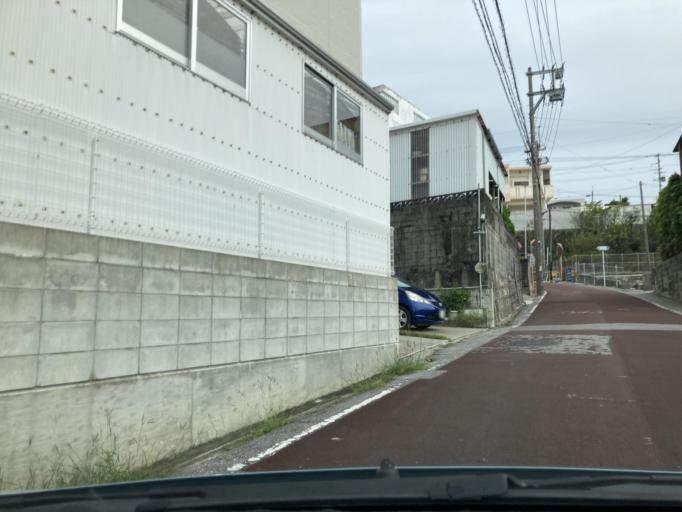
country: JP
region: Okinawa
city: Itoman
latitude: 26.1443
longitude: 127.6770
